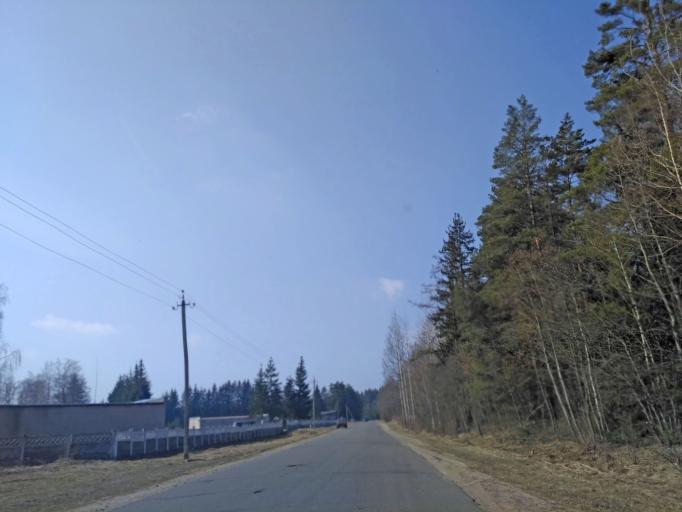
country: BY
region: Minsk
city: Horad Barysaw
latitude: 54.2462
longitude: 28.4573
